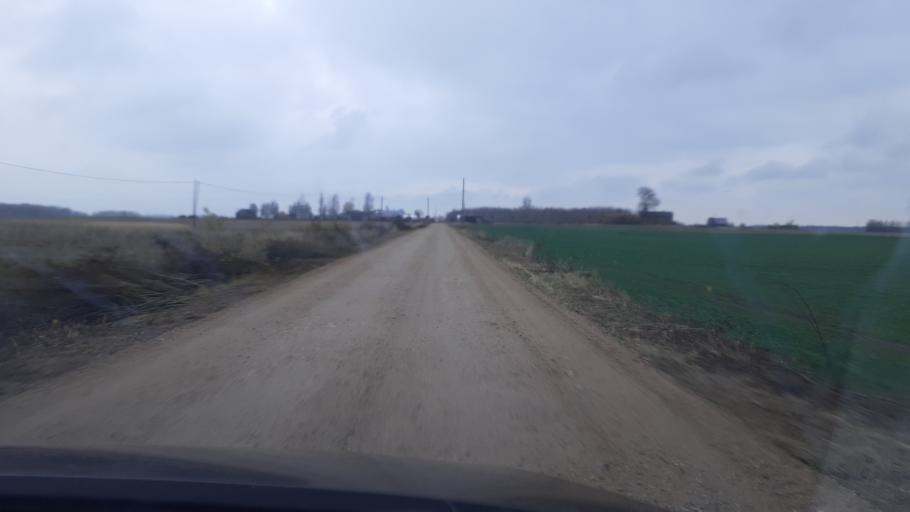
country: LV
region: Talsu Rajons
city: Sabile
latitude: 56.9372
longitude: 22.4185
